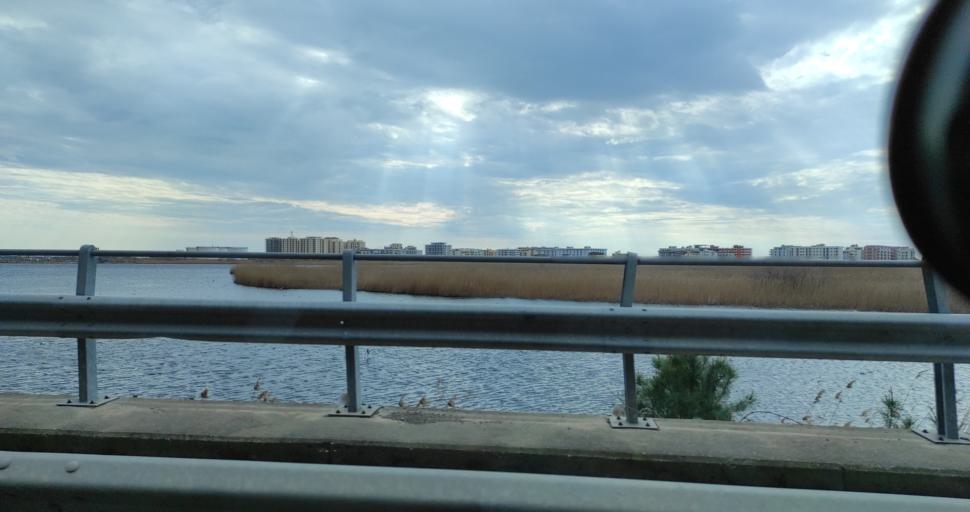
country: AL
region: Lezhe
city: Shengjin
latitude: 41.8051
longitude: 19.6124
